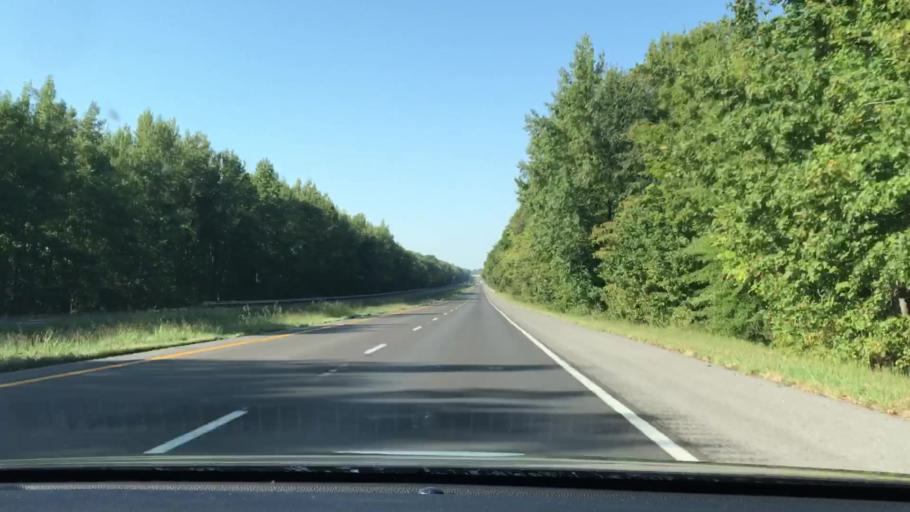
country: US
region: Kentucky
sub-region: Fulton County
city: Fulton
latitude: 36.6014
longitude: -88.7997
